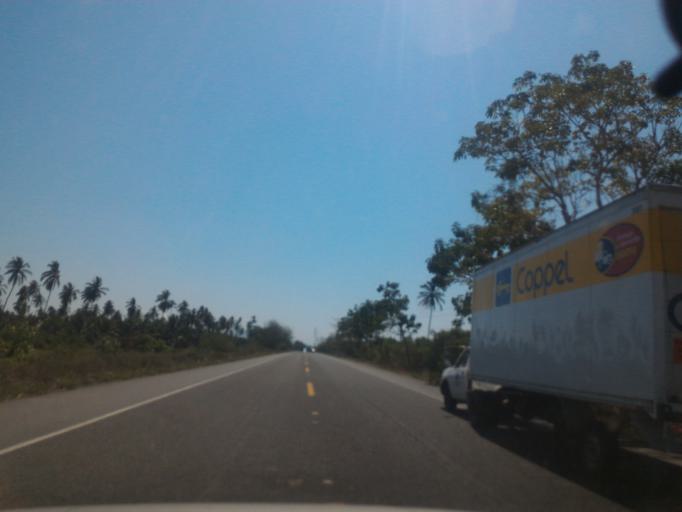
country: MX
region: Colima
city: Tecoman
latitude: 18.8421
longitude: -103.8234
